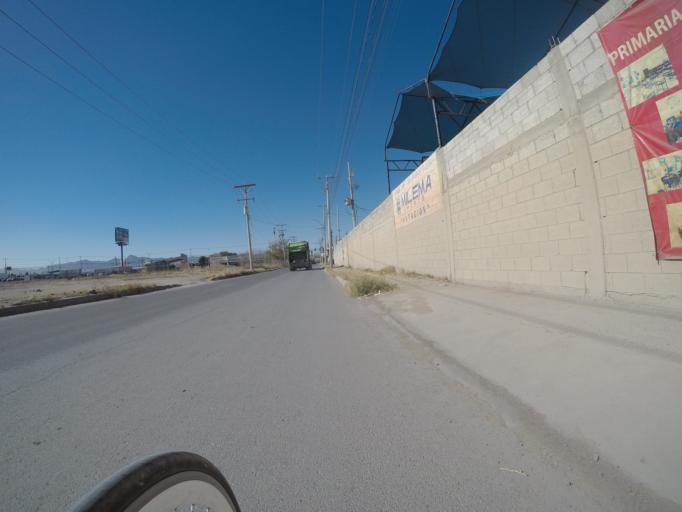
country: MX
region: Chihuahua
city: Ciudad Juarez
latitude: 31.6961
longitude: -106.4026
